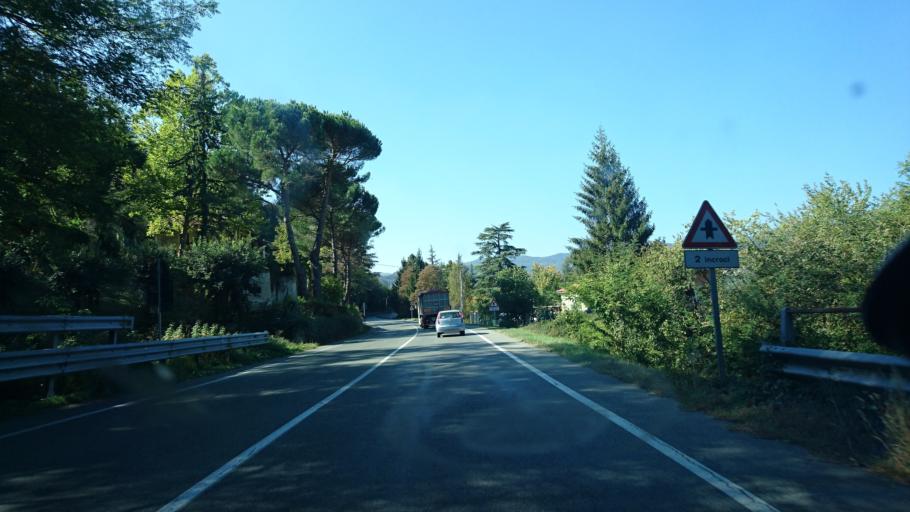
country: IT
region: Piedmont
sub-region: Provincia di Alessandria
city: Spigno Monferrato
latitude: 44.5411
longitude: 8.3322
